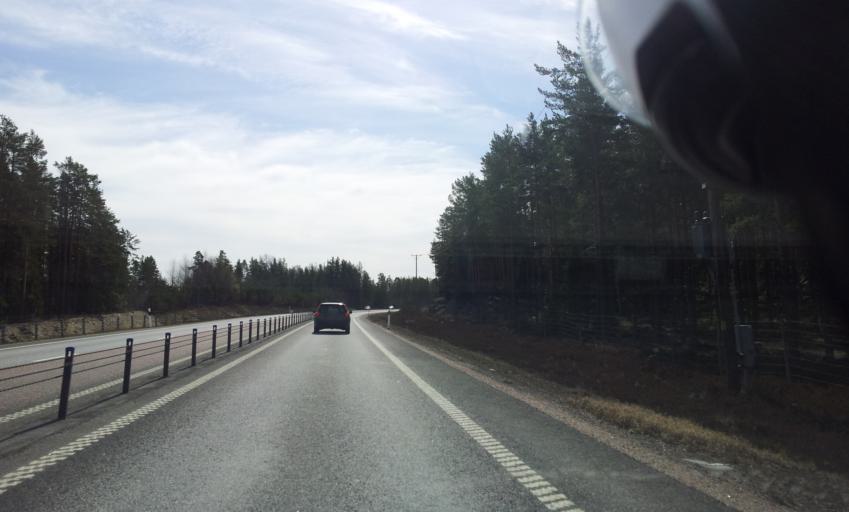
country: SE
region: Gaevleborg
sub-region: Gavle Kommun
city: Norrsundet
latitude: 61.0328
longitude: 16.9723
